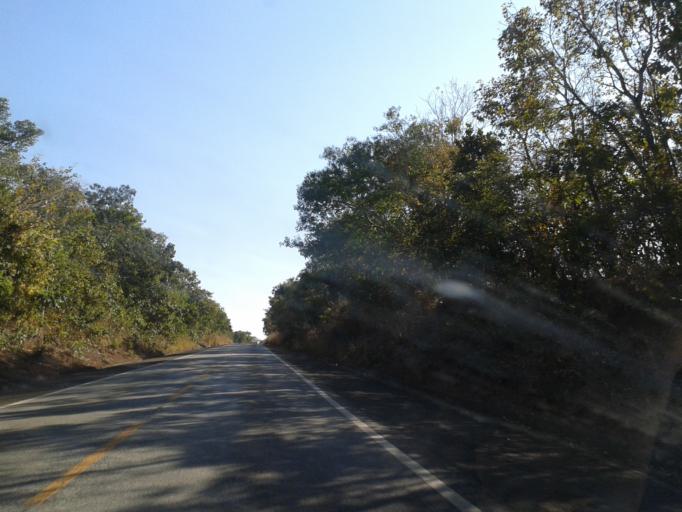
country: BR
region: Goias
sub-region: Mozarlandia
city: Mozarlandia
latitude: -14.9458
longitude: -50.5782
